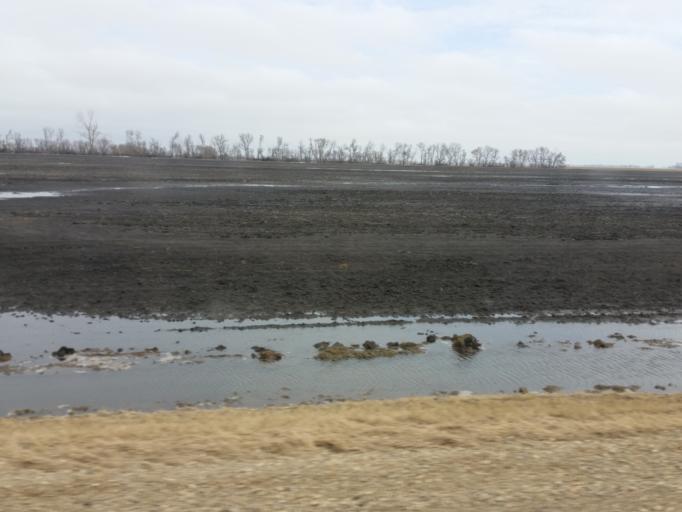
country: US
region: North Dakota
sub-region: Walsh County
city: Grafton
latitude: 48.4145
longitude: -97.3212
